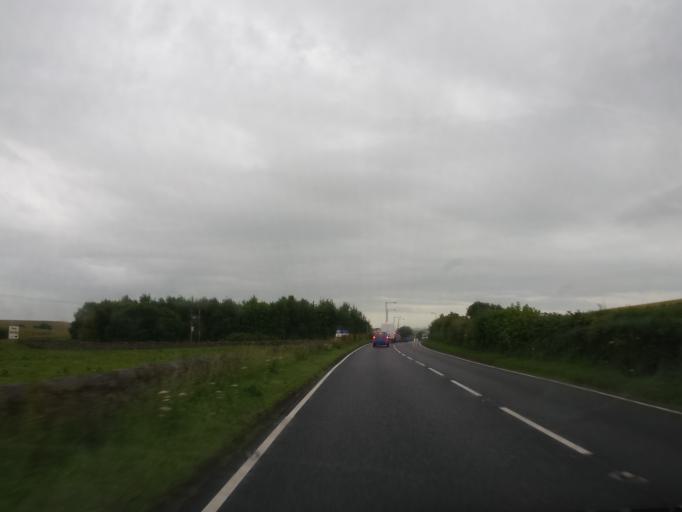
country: GB
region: Scotland
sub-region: Fife
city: Newport-On-Tay
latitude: 56.4176
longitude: -2.9178
